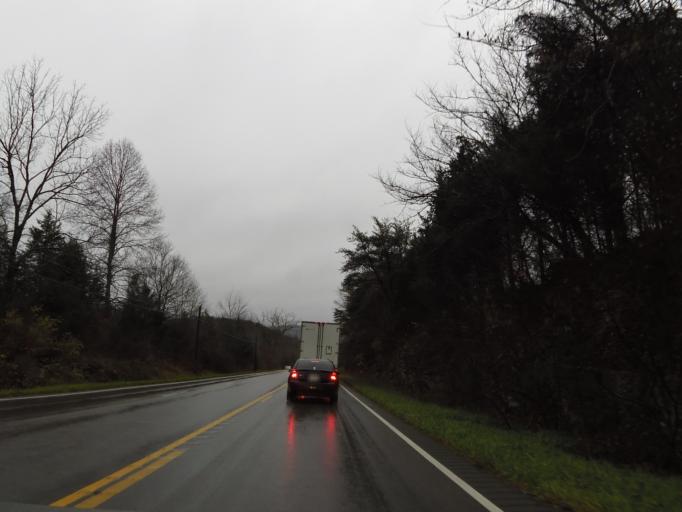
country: US
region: Kentucky
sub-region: Rockcastle County
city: Mount Vernon
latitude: 37.4024
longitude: -84.3352
